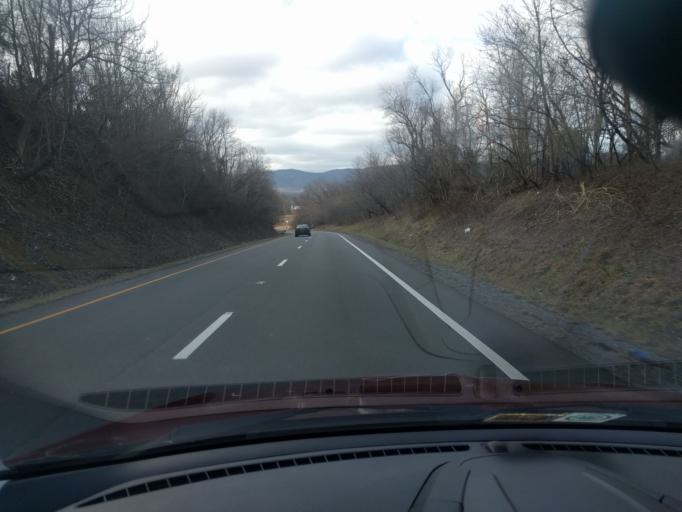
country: US
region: Virginia
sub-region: Botetourt County
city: Blue Ridge
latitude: 37.3670
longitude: -79.6916
